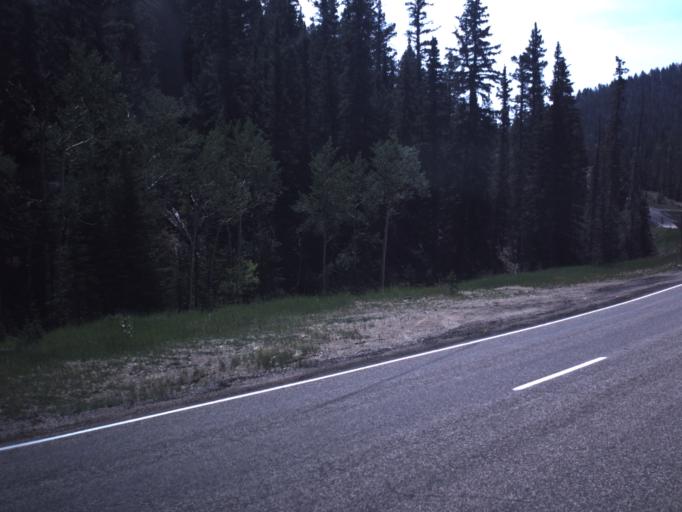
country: US
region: Utah
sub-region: Uintah County
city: Maeser
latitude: 40.7110
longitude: -109.4942
